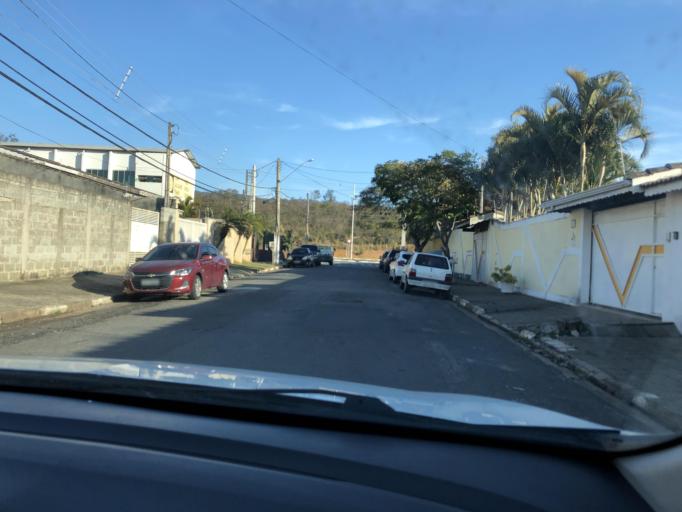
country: BR
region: Sao Paulo
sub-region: Atibaia
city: Atibaia
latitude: -23.1098
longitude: -46.5288
